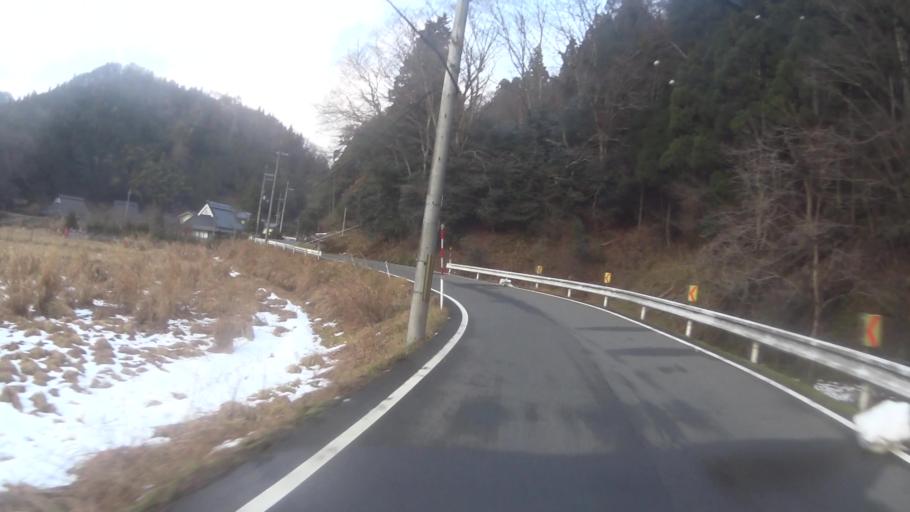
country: JP
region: Kyoto
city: Maizuru
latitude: 35.4123
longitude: 135.4614
